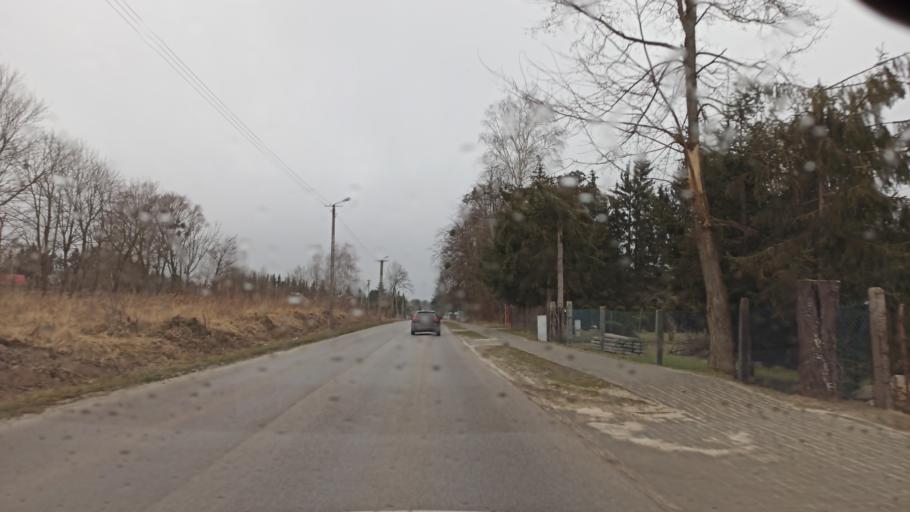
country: PL
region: Lublin Voivodeship
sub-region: Powiat lubelski
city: Bychawa
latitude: 51.0061
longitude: 22.5537
